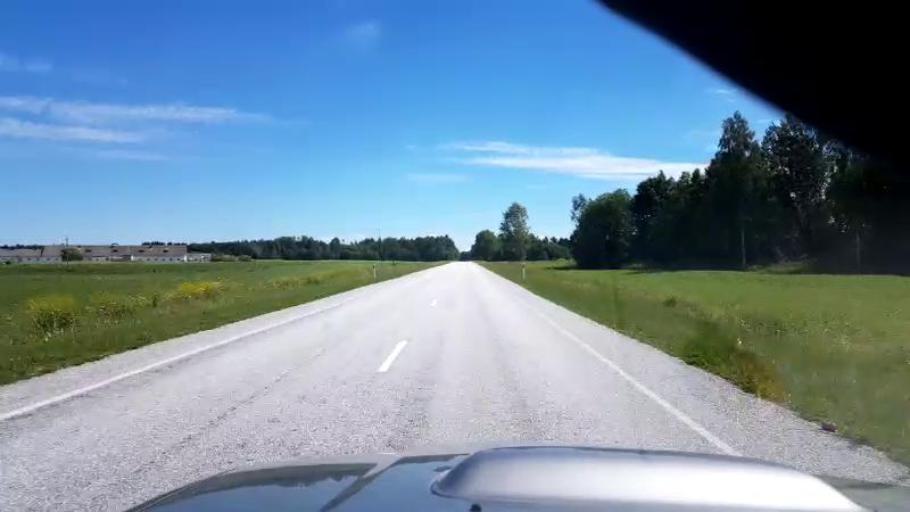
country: EE
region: Laeaene-Virumaa
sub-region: Rakke vald
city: Rakke
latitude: 58.9544
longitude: 26.1735
